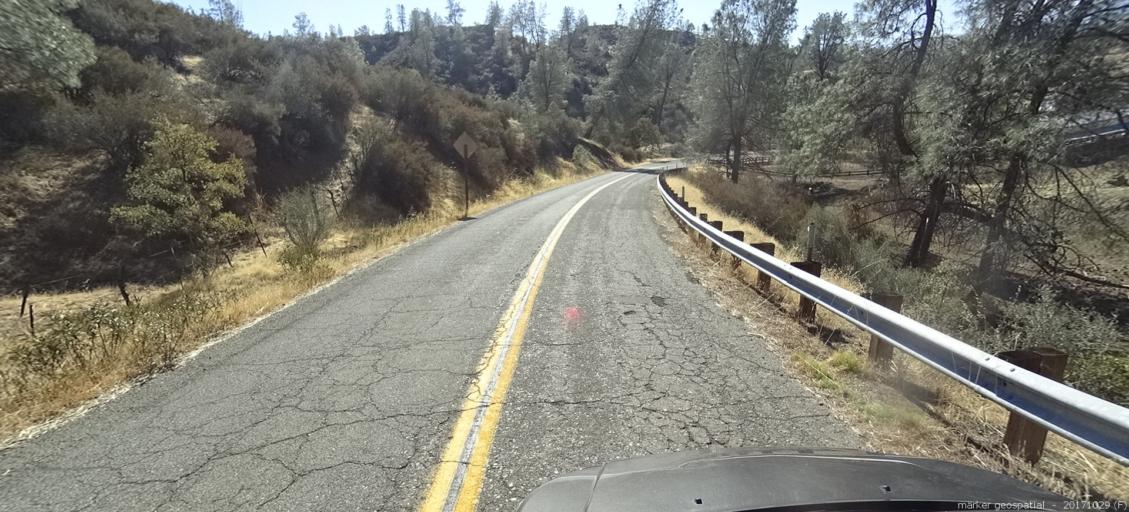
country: US
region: California
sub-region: Trinity County
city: Lewiston
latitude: 40.4196
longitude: -122.7665
